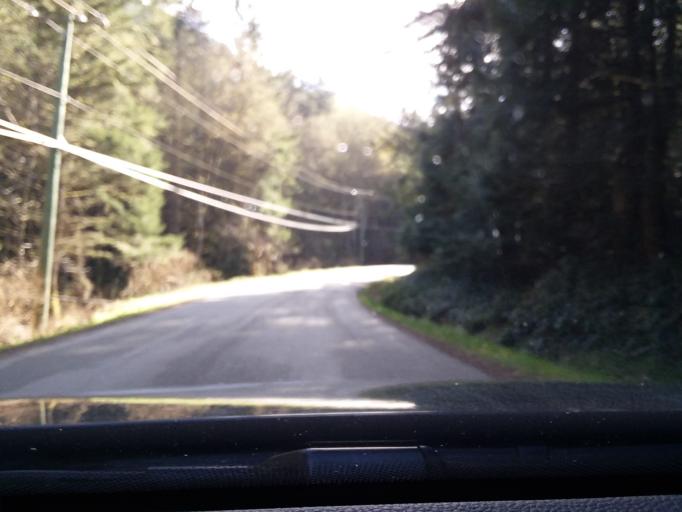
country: CA
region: British Columbia
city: North Saanich
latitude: 48.9205
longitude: -123.4397
